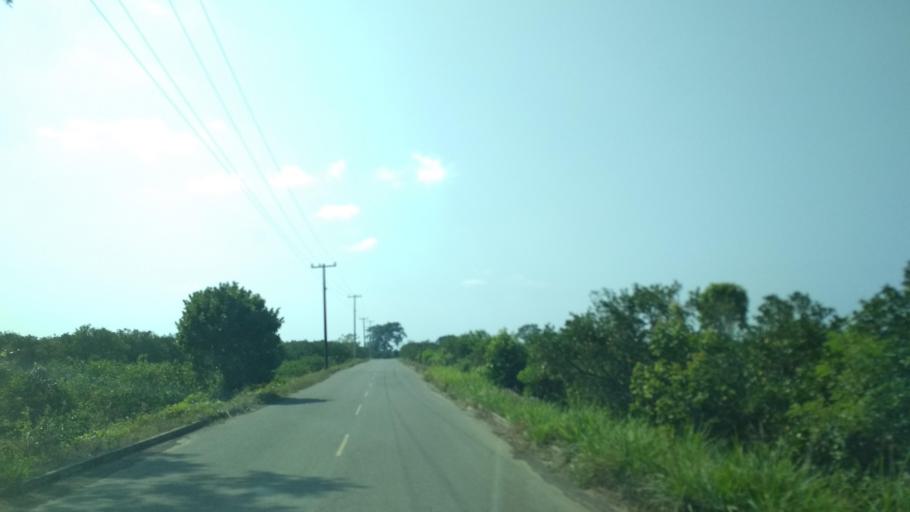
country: MX
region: Puebla
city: San Jose Acateno
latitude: 20.2051
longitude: -97.1784
